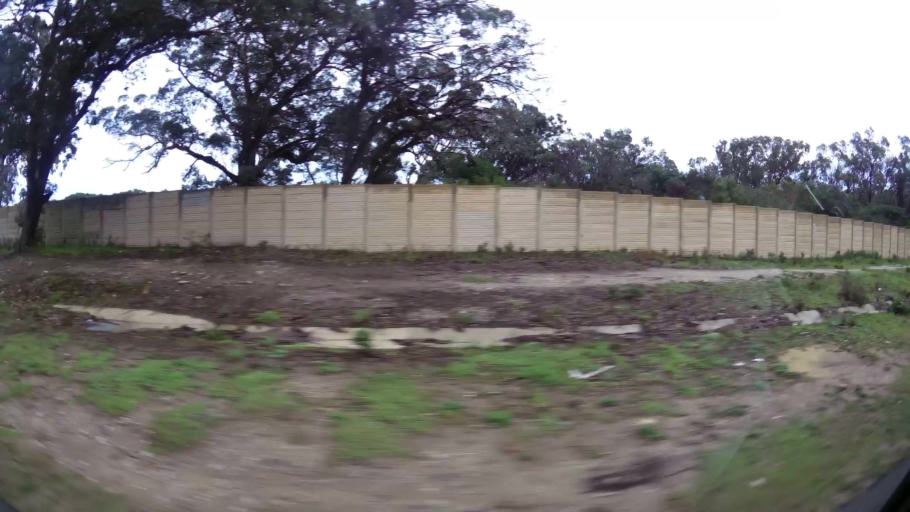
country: ZA
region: Eastern Cape
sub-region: Nelson Mandela Bay Metropolitan Municipality
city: Port Elizabeth
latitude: -33.9931
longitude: 25.5791
